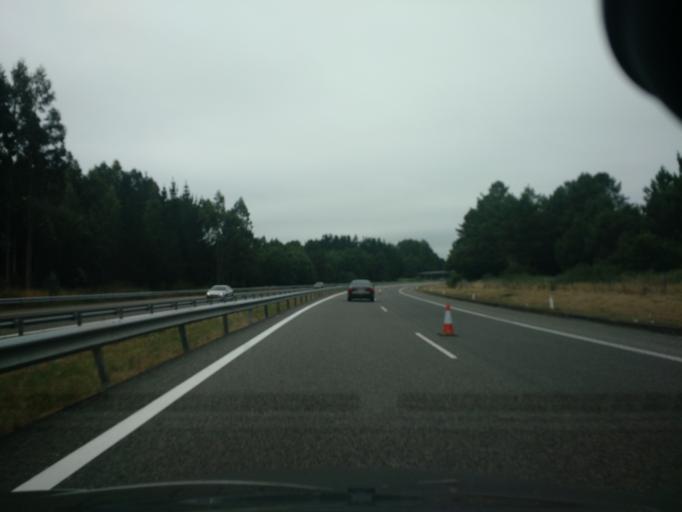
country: ES
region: Galicia
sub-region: Provincia da Coruna
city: Oroso
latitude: 42.9928
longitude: -8.4274
